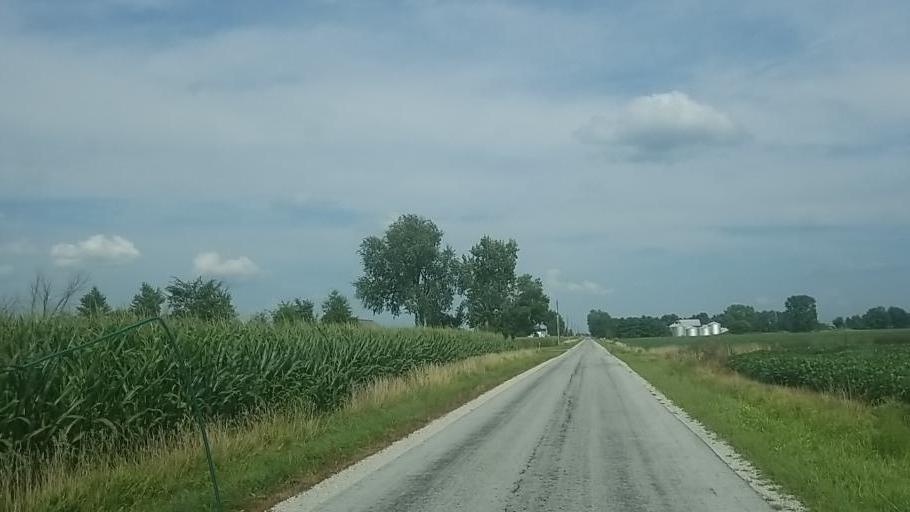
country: US
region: Ohio
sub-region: Hardin County
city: Forest
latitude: 40.8176
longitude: -83.4392
